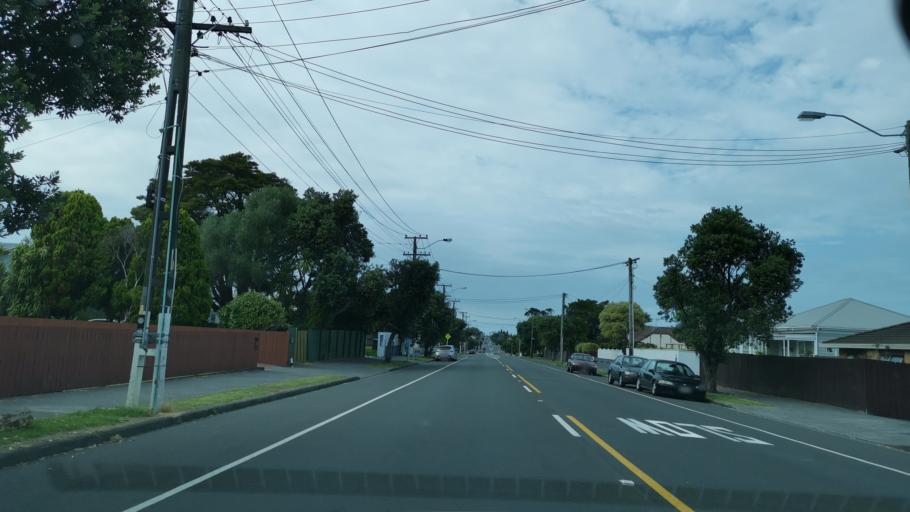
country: NZ
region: Auckland
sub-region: Auckland
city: Rosebank
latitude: -36.8915
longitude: 174.7008
